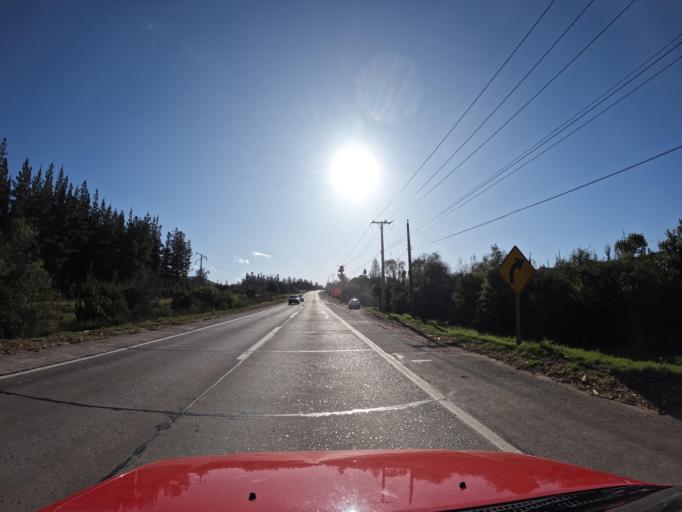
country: CL
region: Maule
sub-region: Provincia de Talca
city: Constitucion
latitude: -35.4435
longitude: -72.3257
